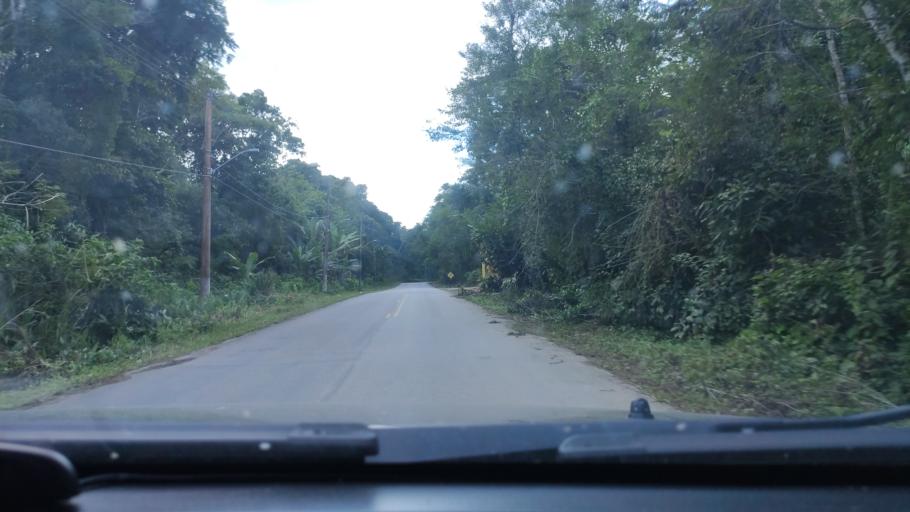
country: BR
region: Sao Paulo
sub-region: Sao Sebastiao
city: Sao Sebastiao
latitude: -23.7094
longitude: -45.4945
